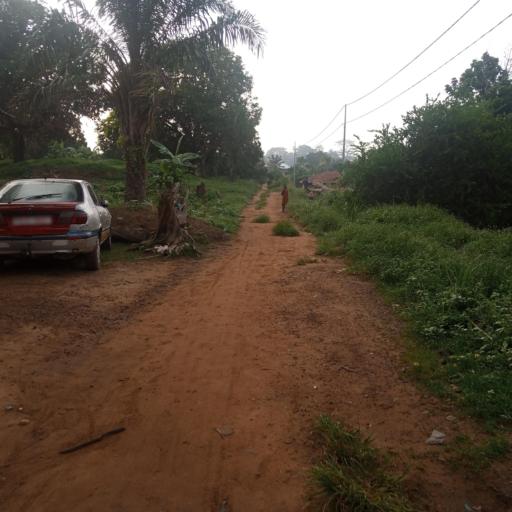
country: SL
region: Eastern Province
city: Pendembu
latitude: 8.0980
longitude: -10.6929
